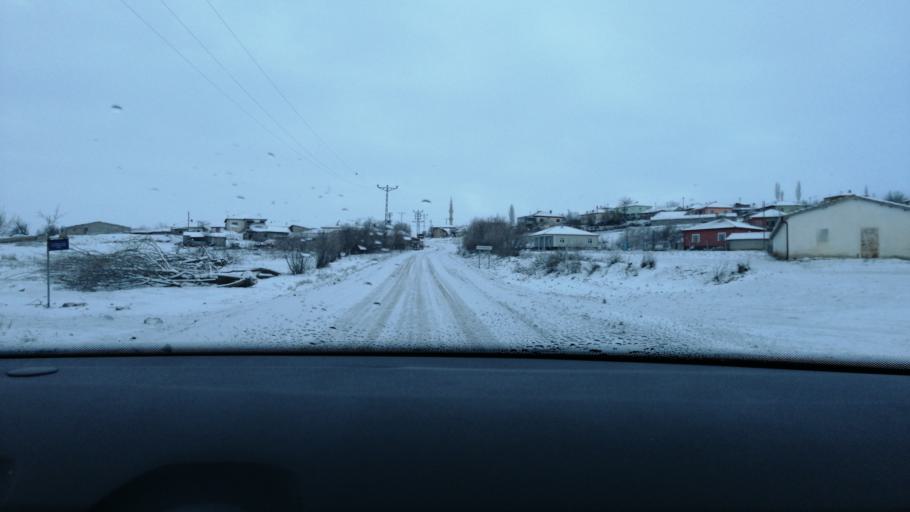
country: TR
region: Aksaray
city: Agacoren
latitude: 38.9373
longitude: 33.9483
